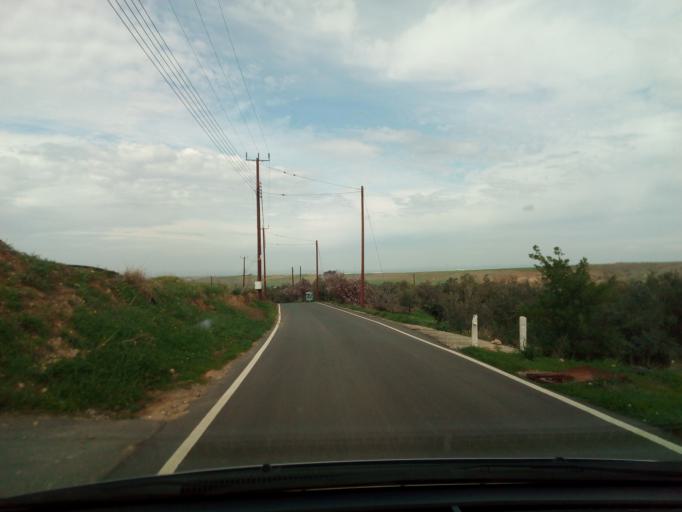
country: CY
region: Lefkosia
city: Astromeritis
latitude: 35.0826
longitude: 32.9966
